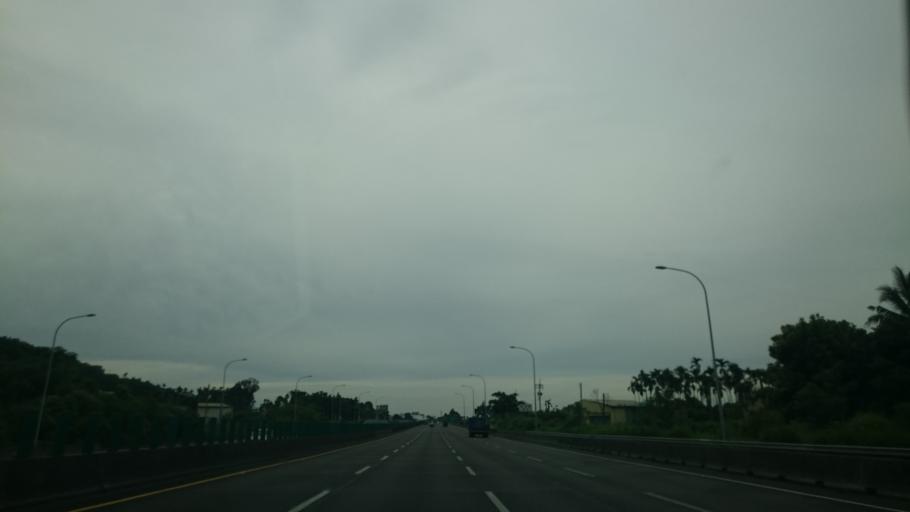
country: TW
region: Taiwan
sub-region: Nantou
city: Nantou
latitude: 23.8724
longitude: 120.7058
